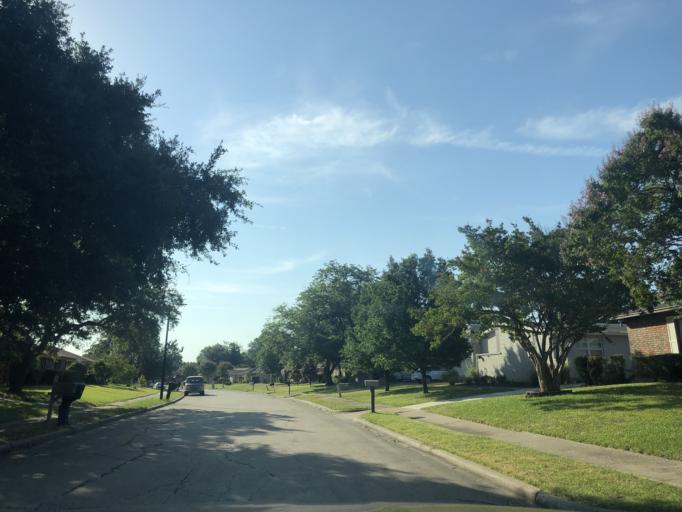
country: US
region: Texas
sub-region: Dallas County
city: Garland
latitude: 32.8555
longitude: -96.6305
